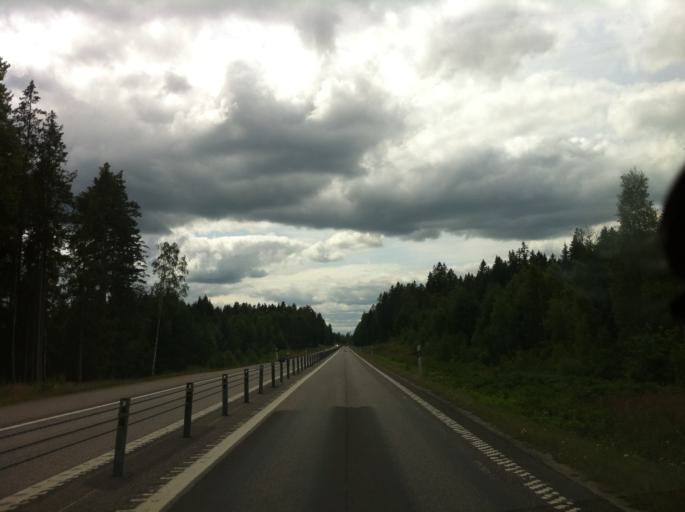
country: SE
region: Kalmar
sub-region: Nybro Kommun
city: Nybro
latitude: 56.7142
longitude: 15.7746
